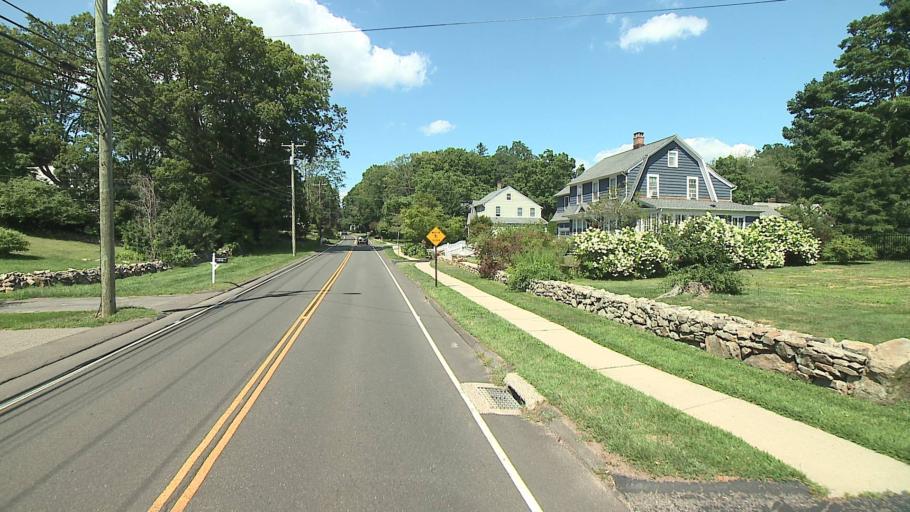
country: US
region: Connecticut
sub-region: Fairfield County
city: Trumbull
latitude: 41.2489
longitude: -73.1624
